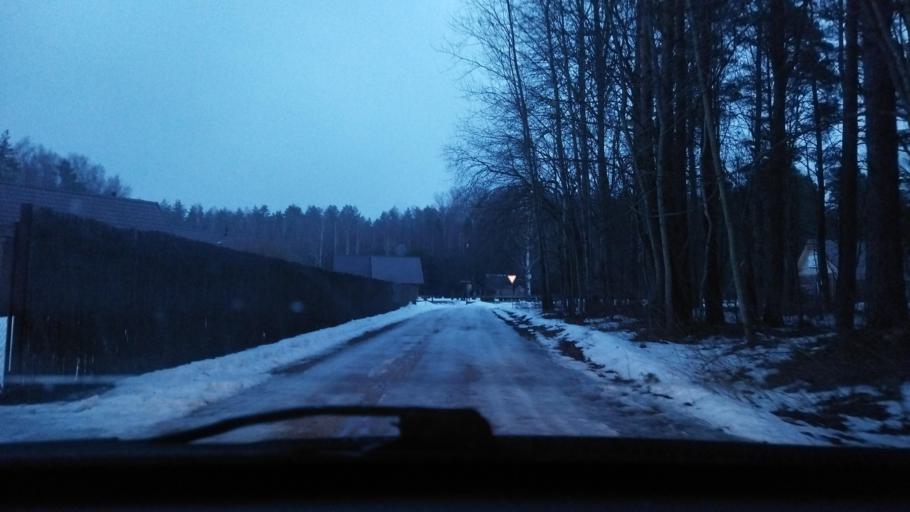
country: BY
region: Minsk
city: Svir
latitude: 54.9395
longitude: 26.4043
